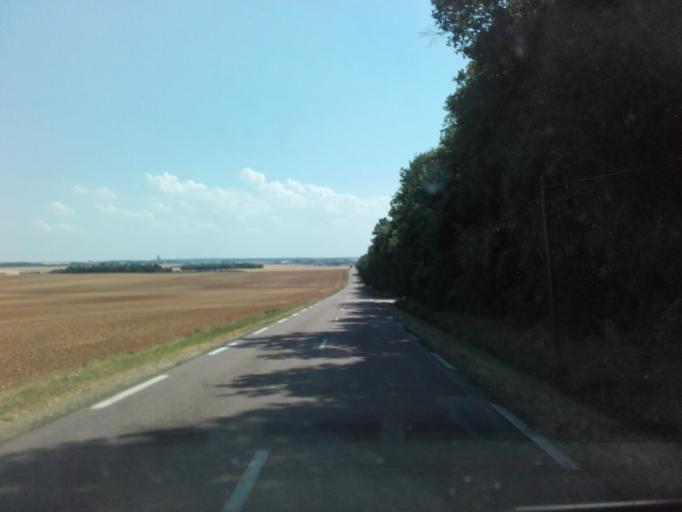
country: FR
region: Bourgogne
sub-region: Departement de l'Yonne
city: Joux-la-Ville
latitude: 47.7009
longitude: 3.8594
